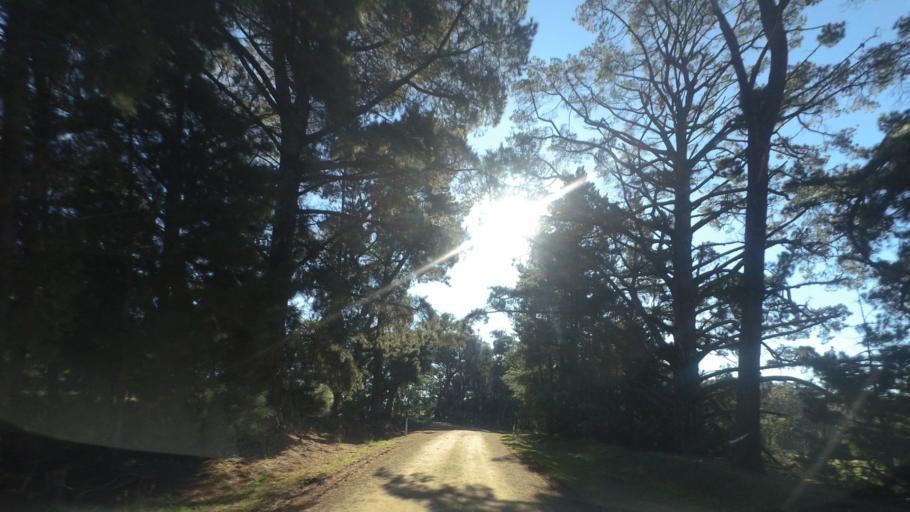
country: AU
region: Victoria
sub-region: Mount Alexander
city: Castlemaine
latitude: -37.2724
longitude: 144.3367
